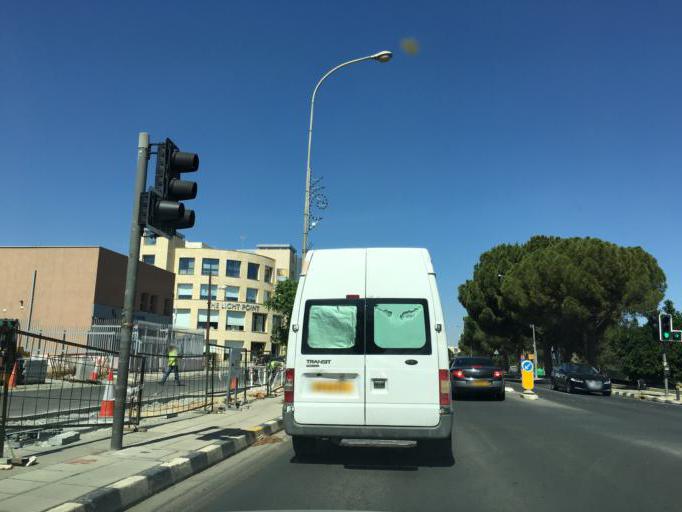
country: CY
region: Lefkosia
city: Nicosia
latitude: 35.1643
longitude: 33.3244
